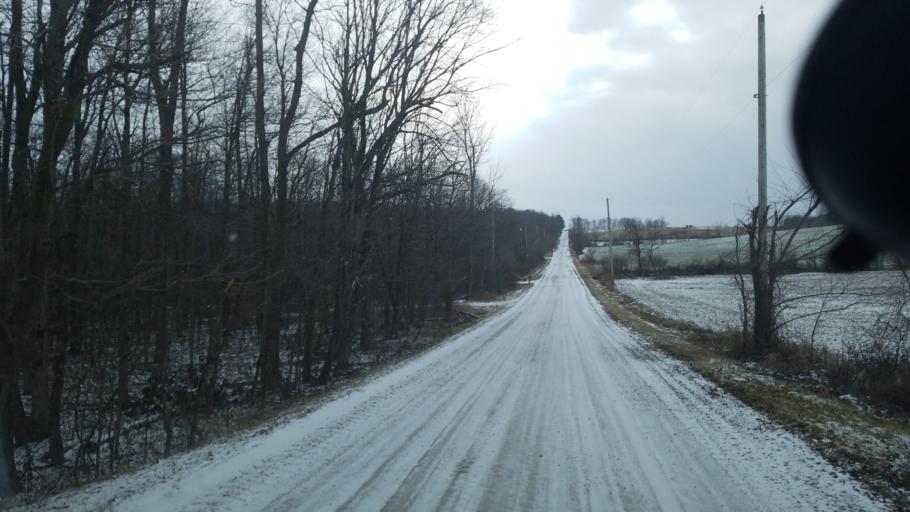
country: US
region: Ohio
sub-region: Morrow County
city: Mount Gilead
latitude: 40.5630
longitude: -82.7101
